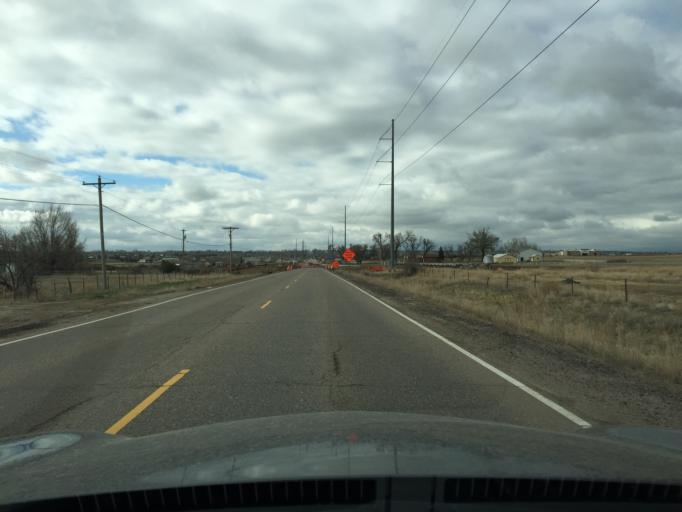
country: US
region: Colorado
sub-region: Adams County
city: Northglenn
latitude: 39.9642
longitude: -104.9784
